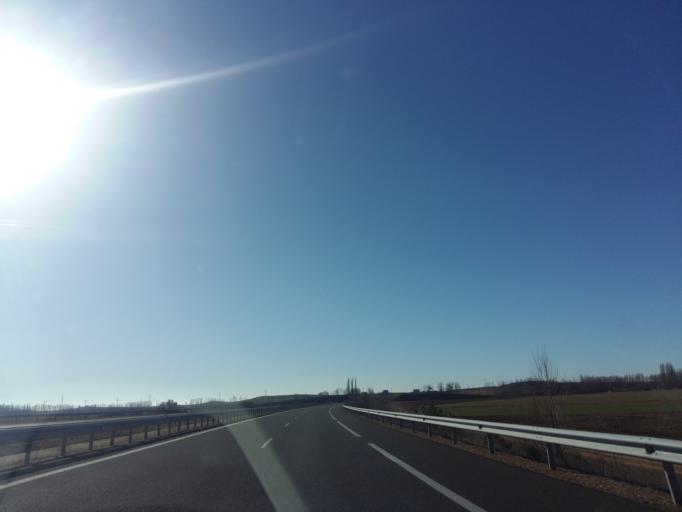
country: ES
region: Castille and Leon
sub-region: Provincia de Palencia
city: Abia de las Torres
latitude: 42.4269
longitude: -4.3898
